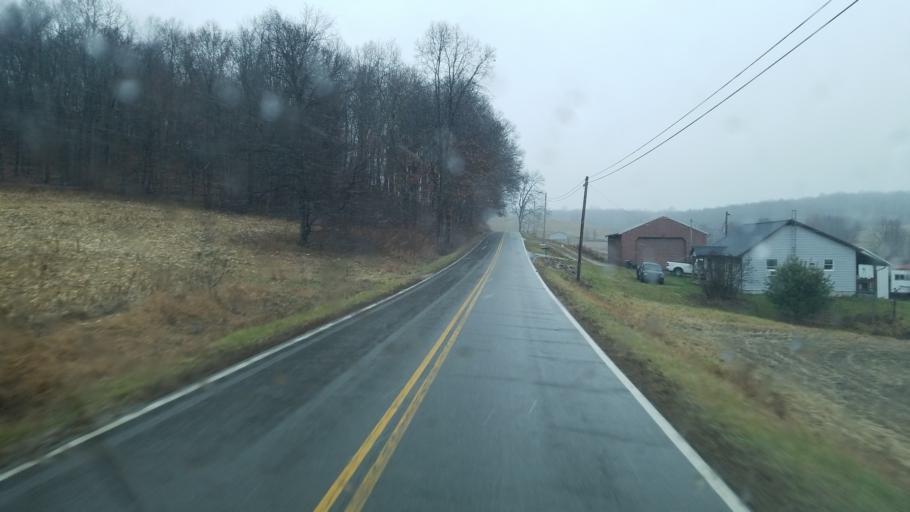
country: US
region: Ohio
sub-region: Licking County
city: Utica
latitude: 40.1877
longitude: -82.3375
